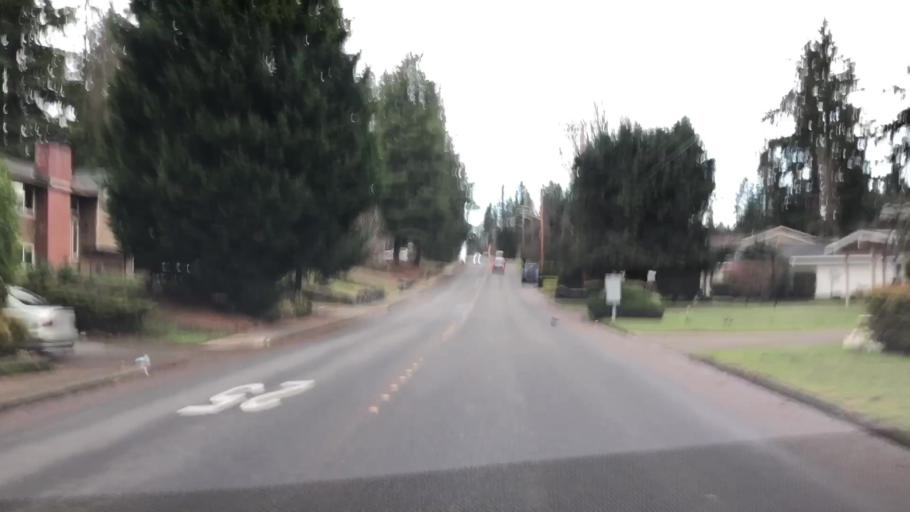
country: US
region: Washington
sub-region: King County
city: West Lake Sammamish
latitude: 47.6080
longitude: -122.1213
